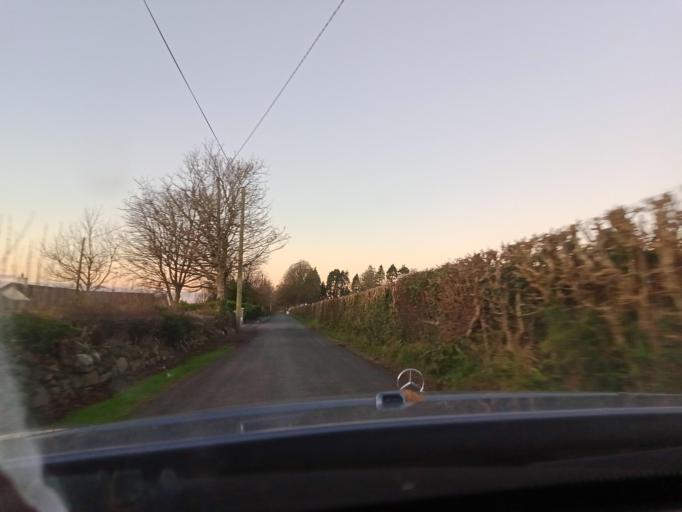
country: IE
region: Leinster
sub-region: Kilkenny
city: Thomastown
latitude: 52.4697
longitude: -7.0979
